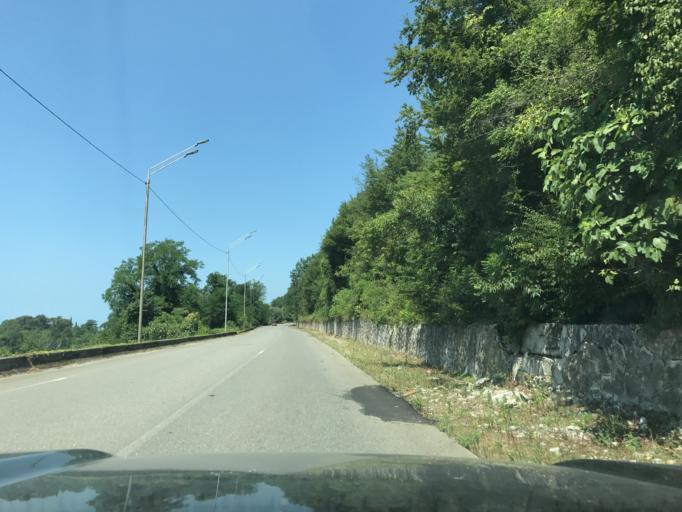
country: GE
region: Abkhazia
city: Gagra
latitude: 43.2771
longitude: 40.2845
